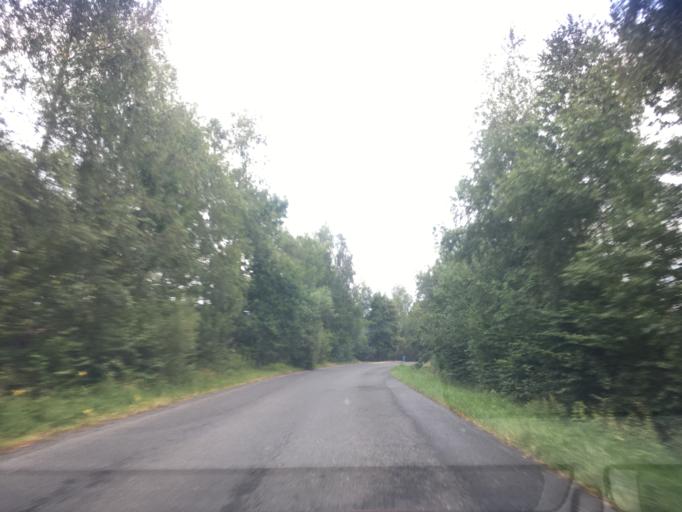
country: PL
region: Lesser Poland Voivodeship
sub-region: Powiat myslenicki
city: Brzaczowice
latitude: 49.8588
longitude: 20.0598
